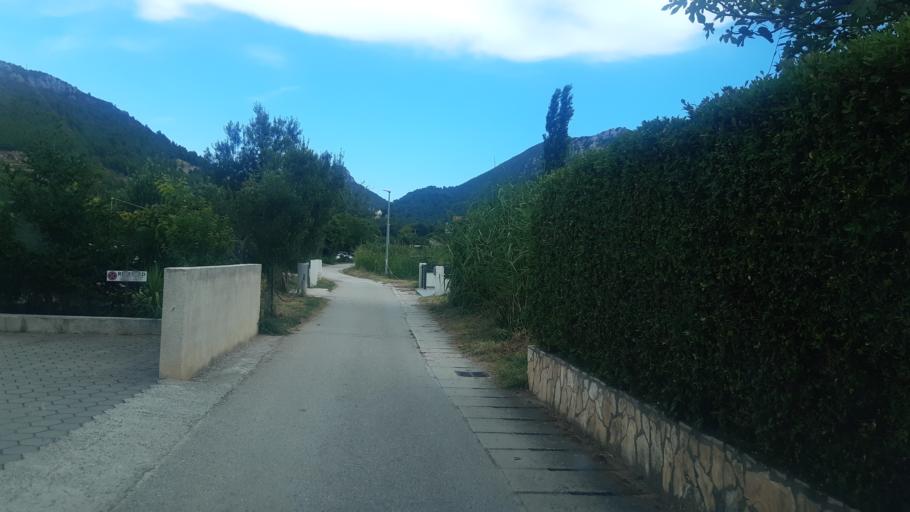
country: HR
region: Dubrovacko-Neretvanska
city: Blato
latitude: 42.8896
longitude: 17.4543
